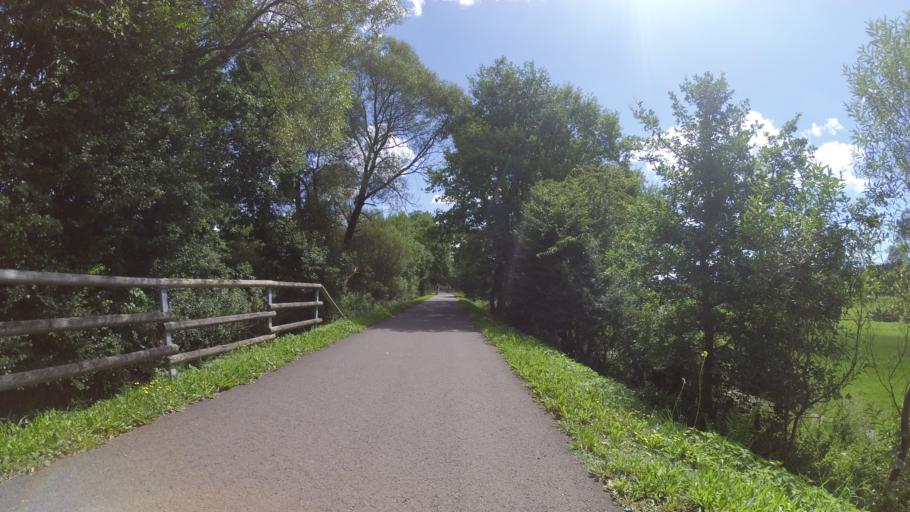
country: DE
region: Saarland
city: Namborn
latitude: 49.4914
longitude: 7.1355
